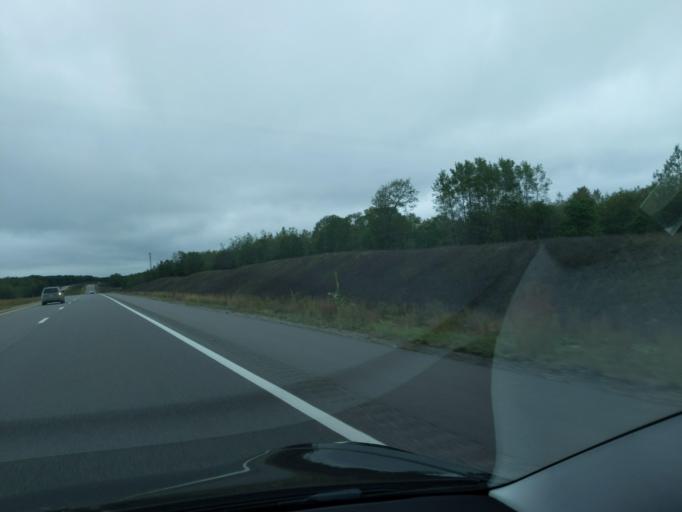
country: US
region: Michigan
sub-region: Wexford County
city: Cadillac
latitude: 44.3195
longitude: -85.3976
